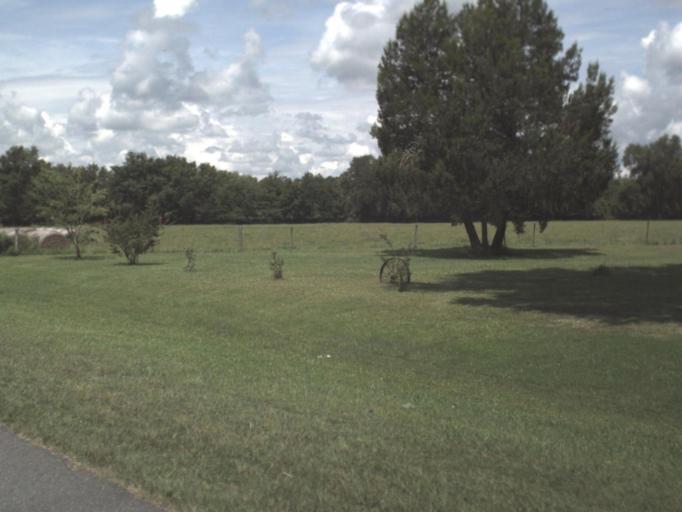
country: US
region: Florida
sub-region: Alachua County
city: Alachua
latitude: 29.8275
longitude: -82.4247
